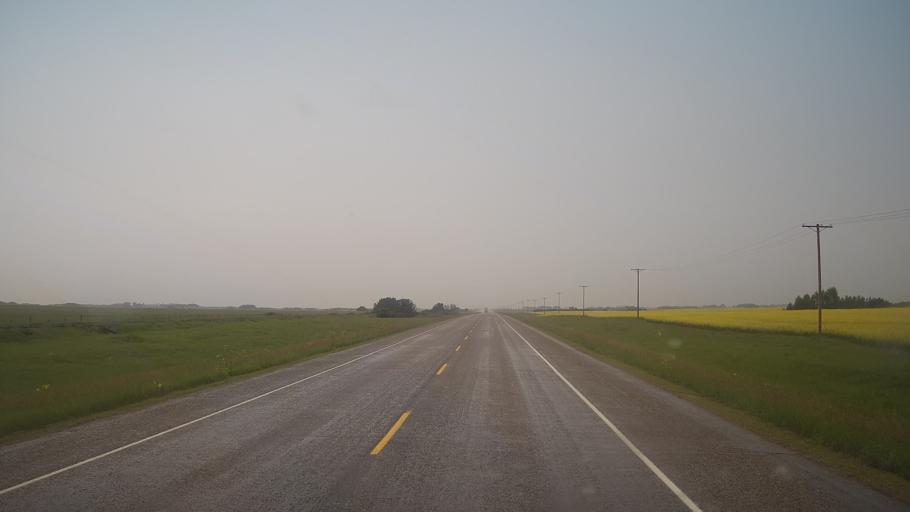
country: CA
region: Saskatchewan
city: Biggar
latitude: 52.1496
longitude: -108.2264
